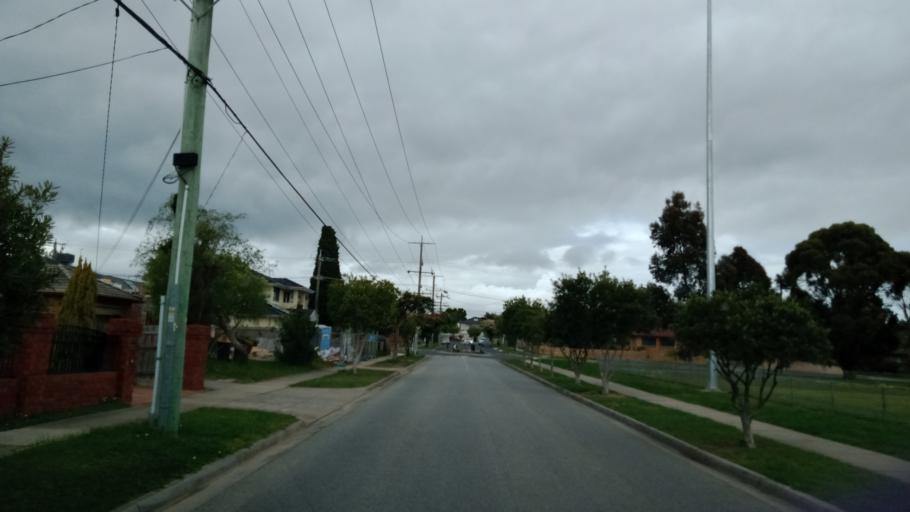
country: AU
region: Victoria
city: Burwood East
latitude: -37.8706
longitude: 145.1608
